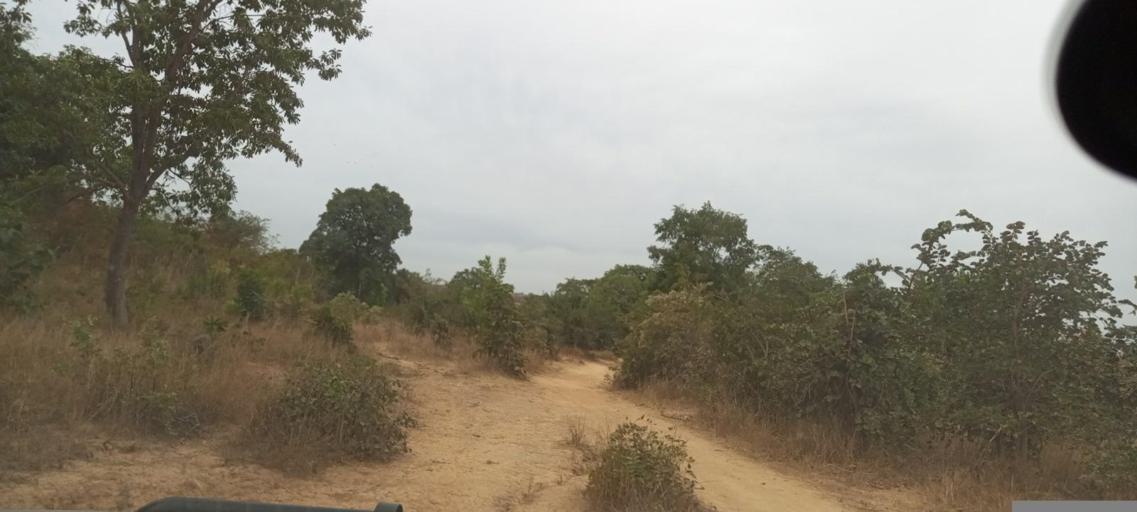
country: ML
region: Koulikoro
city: Kati
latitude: 12.7701
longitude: -8.3742
